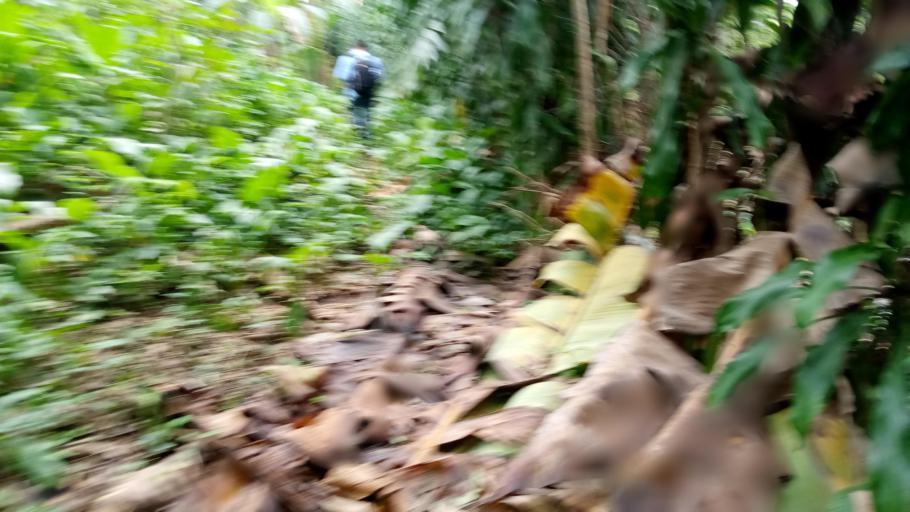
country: GT
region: Retalhuleu
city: San Martin Zapotitlan
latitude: 14.6028
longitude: -91.6029
